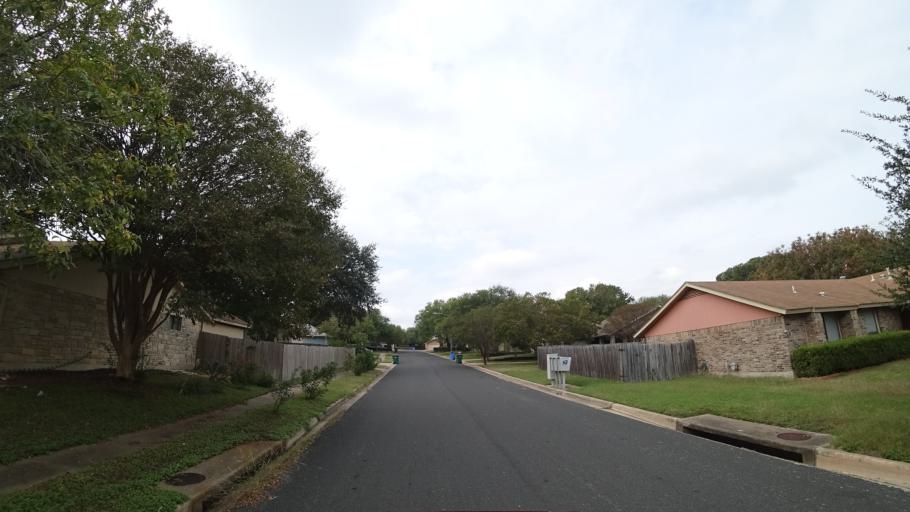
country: US
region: Texas
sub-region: Travis County
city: Wells Branch
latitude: 30.4393
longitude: -97.6818
